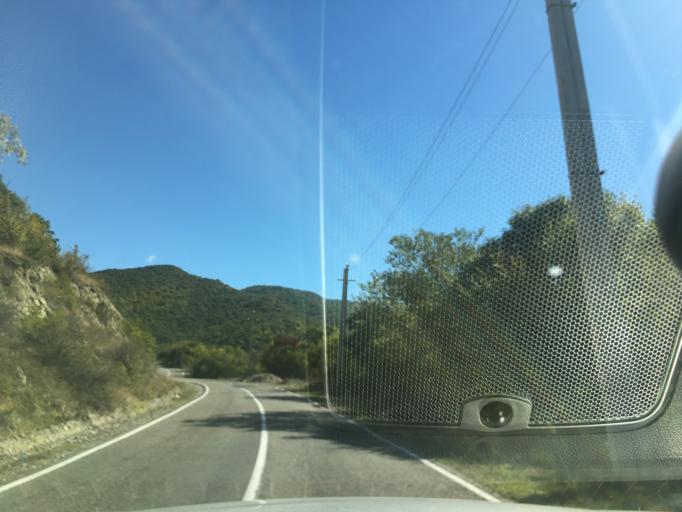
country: GE
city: Zahesi
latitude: 41.8425
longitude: 44.8819
